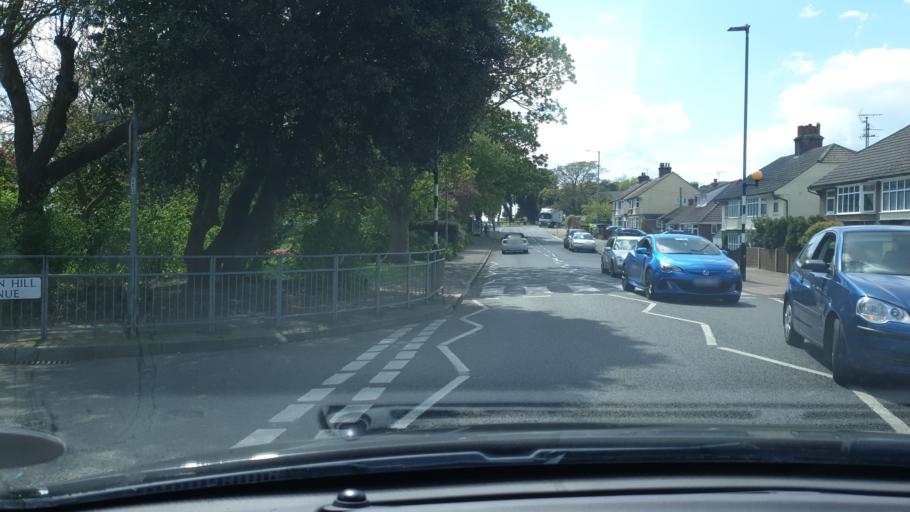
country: GB
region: England
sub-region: Essex
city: Harwich
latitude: 51.9402
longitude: 1.2863
